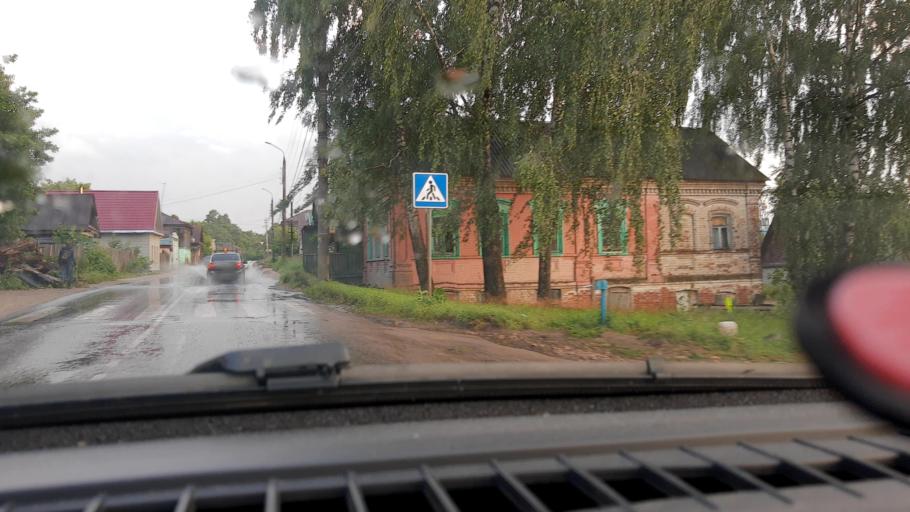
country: RU
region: Nizjnij Novgorod
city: Gorodets
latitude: 56.6540
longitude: 43.4646
